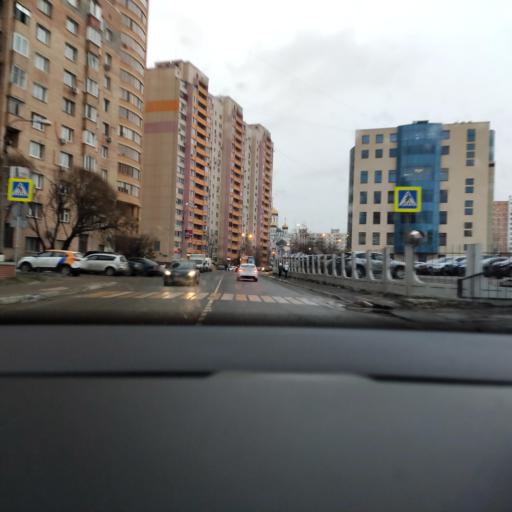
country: RU
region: Moskovskaya
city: Reutov
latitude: 55.7572
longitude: 37.8622
